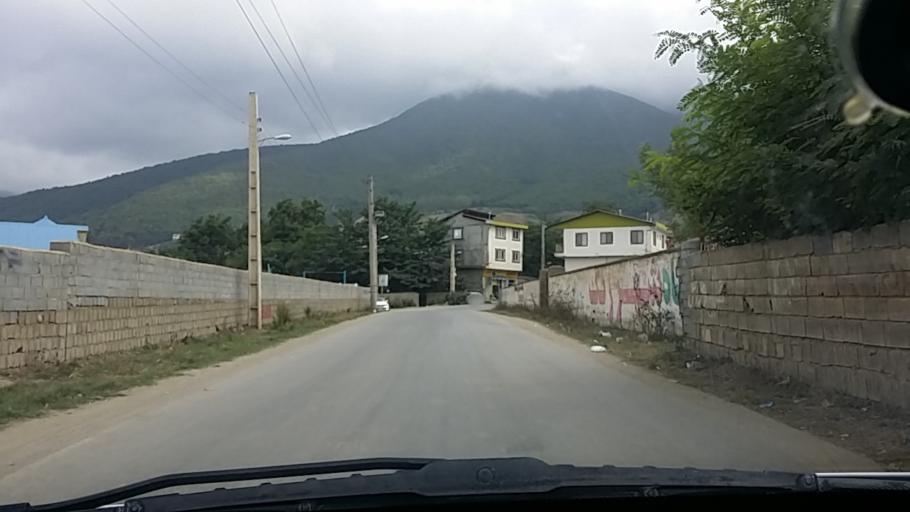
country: IR
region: Mazandaran
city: `Abbasabad
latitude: 36.5097
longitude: 51.1854
